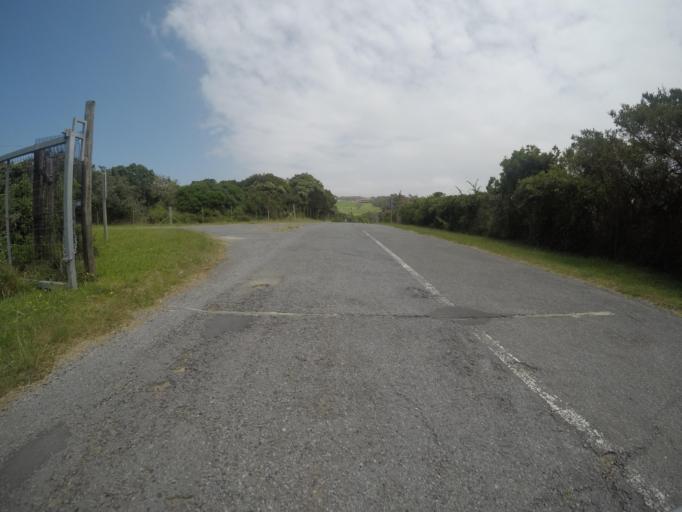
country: ZA
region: Eastern Cape
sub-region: Buffalo City Metropolitan Municipality
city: East London
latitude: -32.9941
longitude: 27.9419
